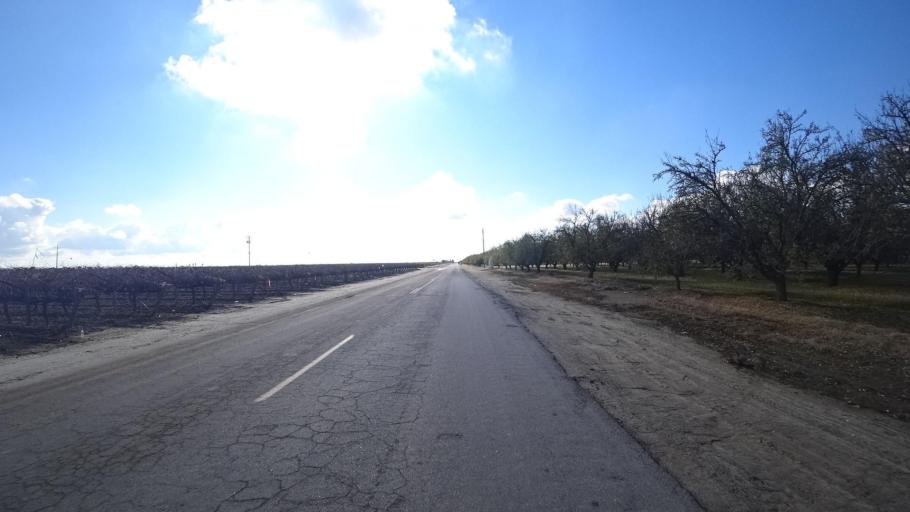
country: US
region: California
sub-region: Kern County
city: McFarland
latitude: 35.6826
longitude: -119.2587
